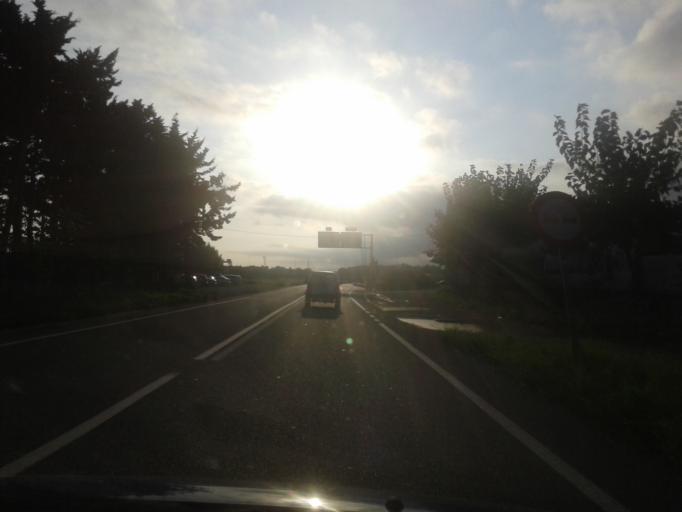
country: ES
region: Catalonia
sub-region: Provincia de Barcelona
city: Cubelles
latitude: 41.2055
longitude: 1.6653
